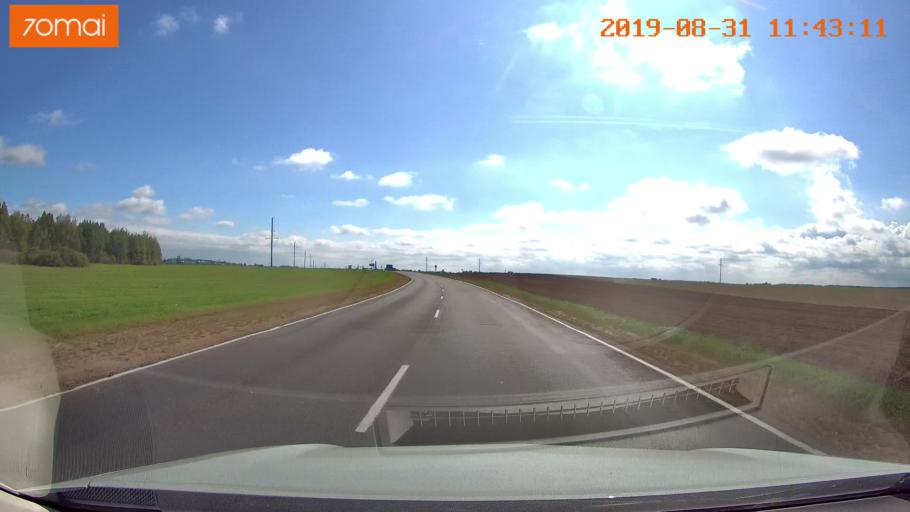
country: BY
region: Mogilev
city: Cherykaw
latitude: 53.5878
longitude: 31.3417
